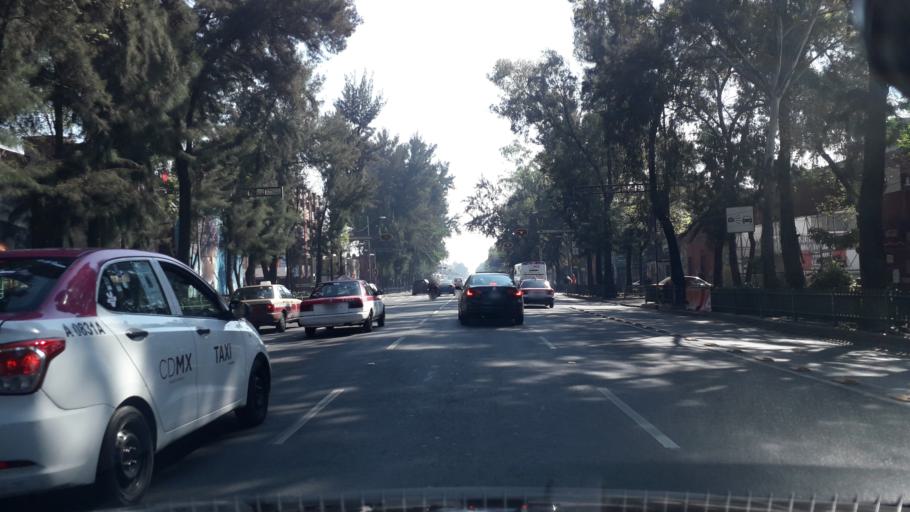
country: MX
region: Mexico City
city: Cuauhtemoc
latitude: 19.4457
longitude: -99.1496
